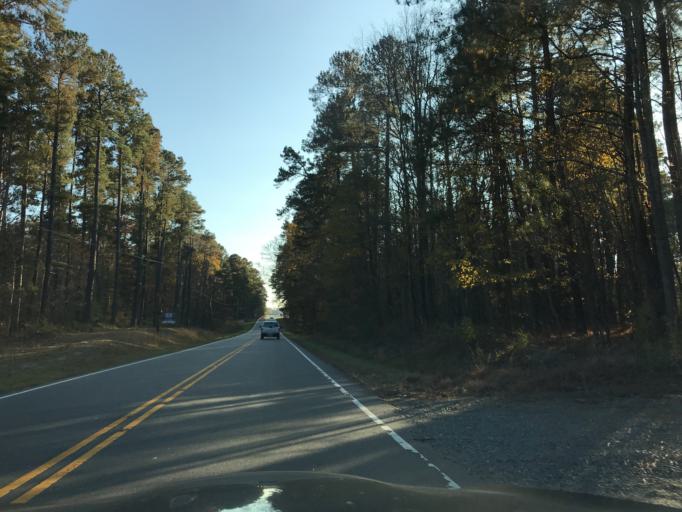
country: US
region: North Carolina
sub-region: Granville County
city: Creedmoor
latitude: 36.0781
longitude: -78.6930
